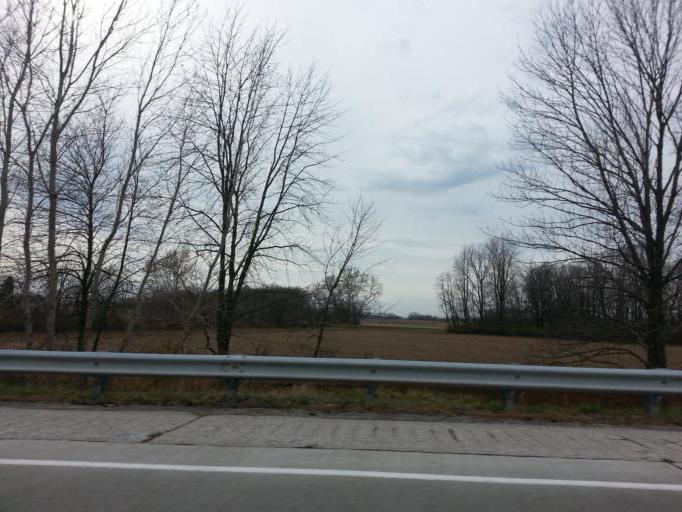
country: US
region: Indiana
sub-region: Decatur County
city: Greensburg
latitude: 39.3508
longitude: -85.4464
